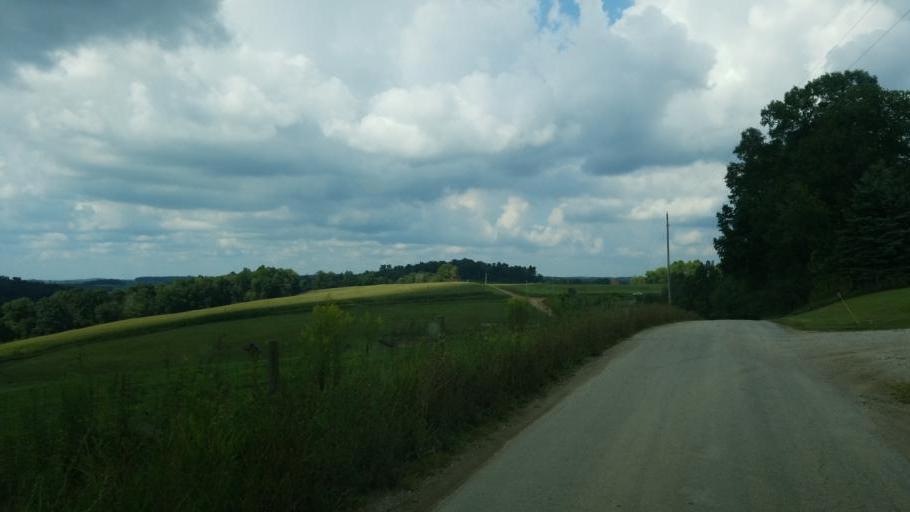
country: US
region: Ohio
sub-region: Knox County
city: Oak Hill
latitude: 40.3960
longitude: -82.2271
